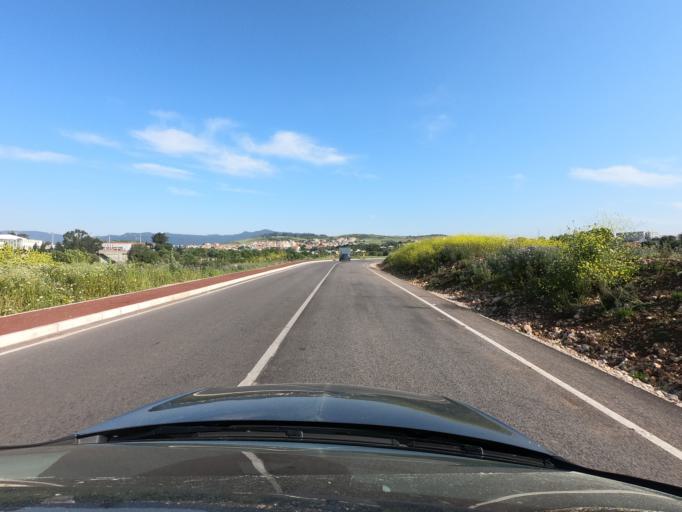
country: PT
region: Lisbon
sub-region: Cascais
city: Parede
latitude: 38.7339
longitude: -9.3573
